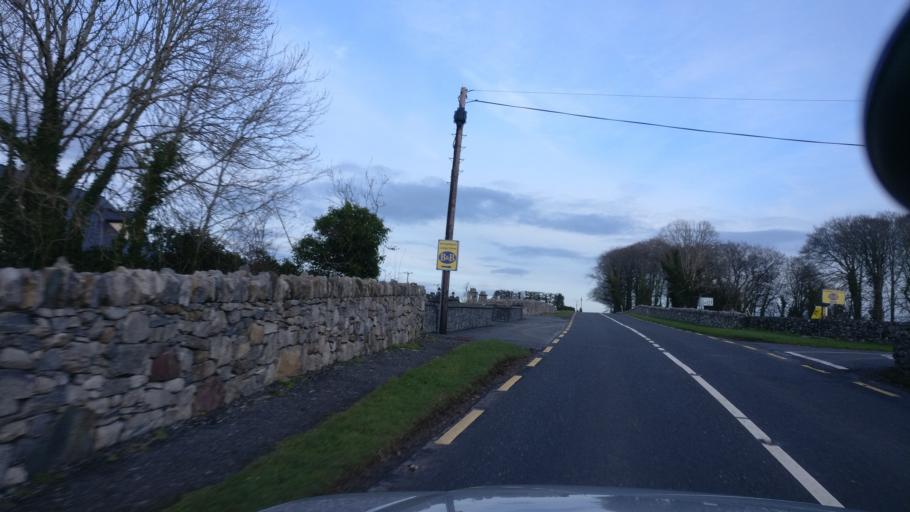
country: IE
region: Connaught
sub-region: Maigh Eo
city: Ballinrobe
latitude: 53.5407
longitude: -9.2593
